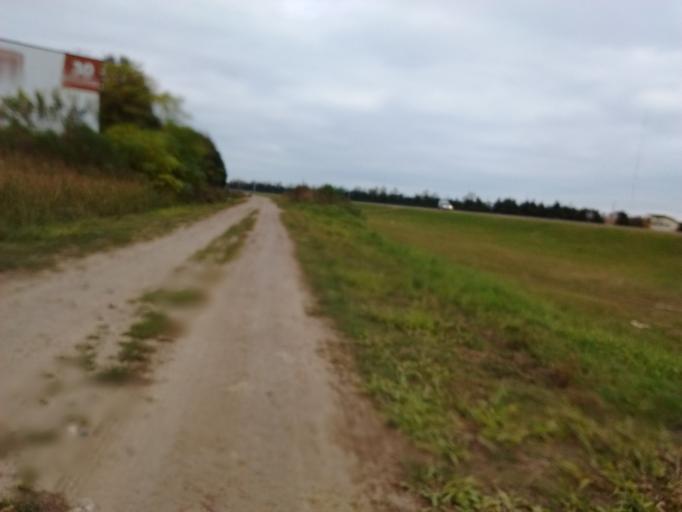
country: AR
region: Santa Fe
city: Funes
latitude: -32.9364
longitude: -60.8293
